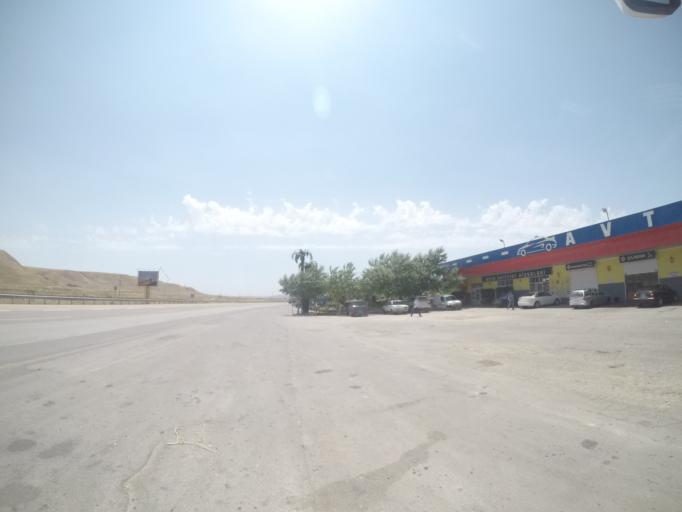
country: AZ
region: Haciqabul
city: Haciqabul
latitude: 40.0203
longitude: 48.9547
